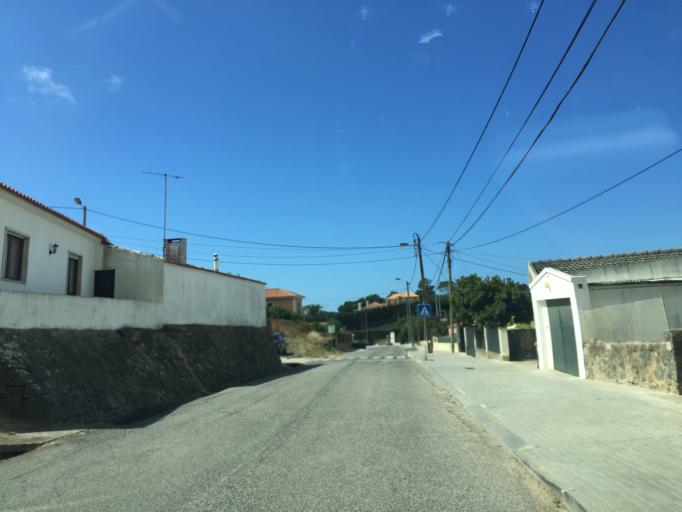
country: PT
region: Lisbon
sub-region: Sintra
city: Colares
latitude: 38.7570
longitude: -9.4461
